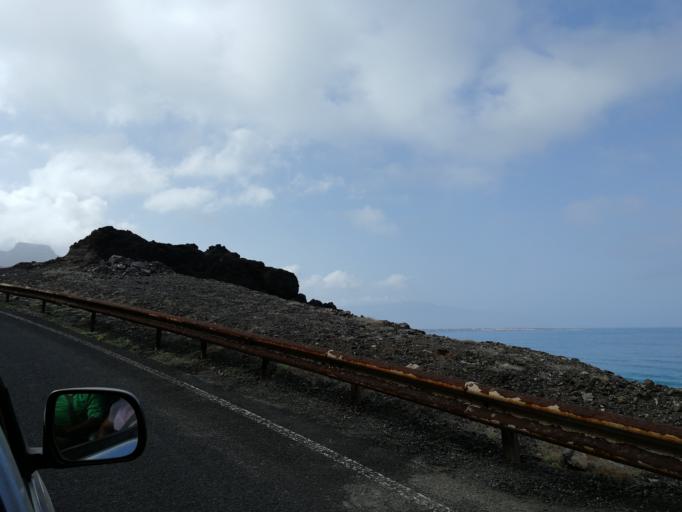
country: CV
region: Sao Vicente
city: Mindelo
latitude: 16.8658
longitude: -24.8953
